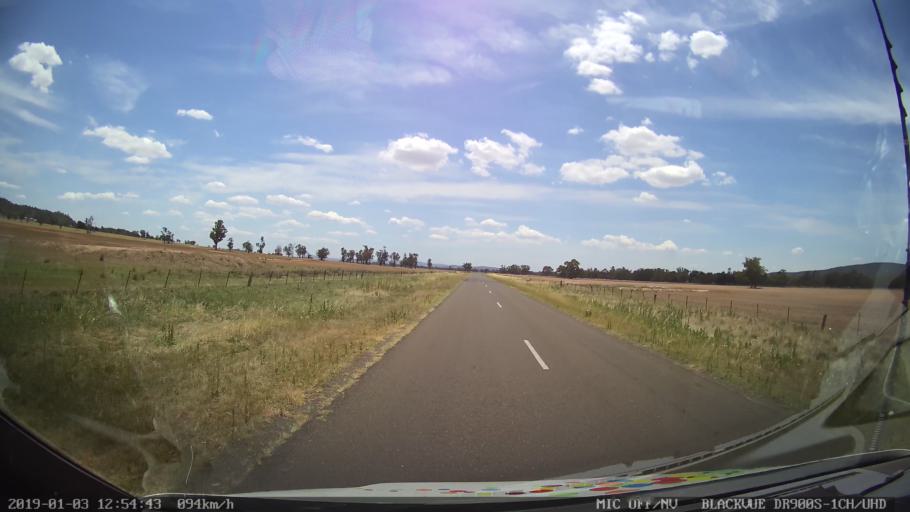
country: AU
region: New South Wales
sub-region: Weddin
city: Grenfell
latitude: -33.6500
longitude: 148.3205
